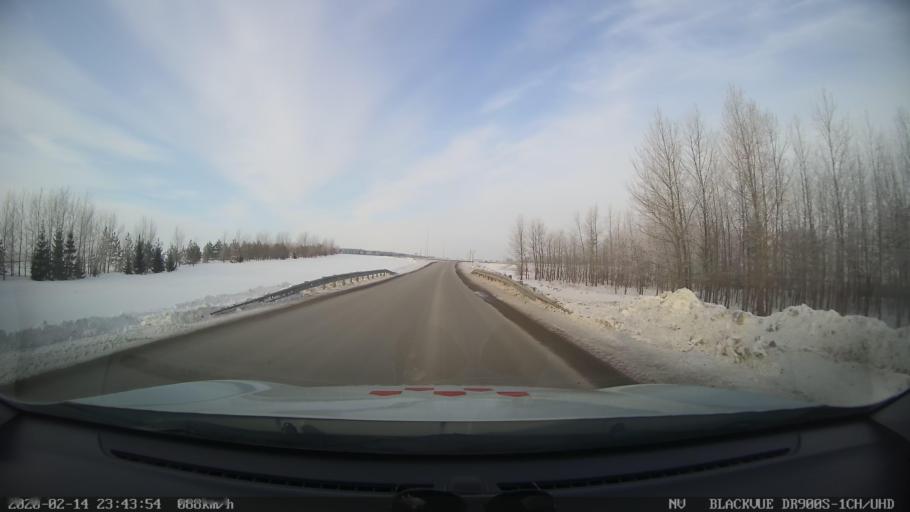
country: RU
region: Tatarstan
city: Kuybyshevskiy Zaton
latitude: 55.2076
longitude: 49.2476
